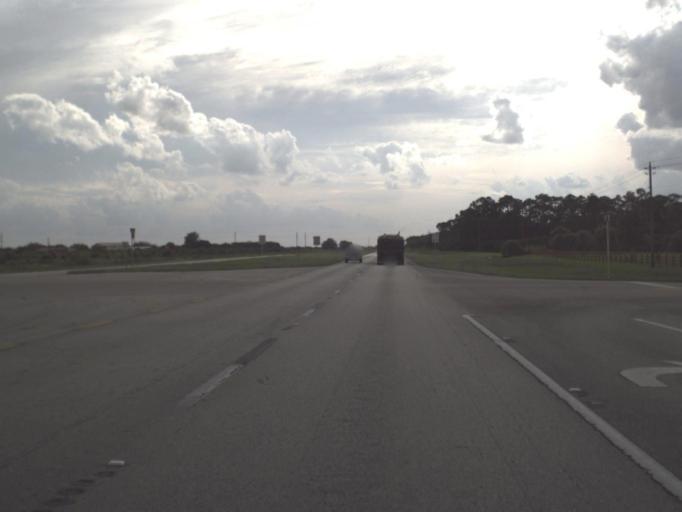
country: US
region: Florida
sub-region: Hendry County
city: LaBelle
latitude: 26.7361
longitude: -81.4733
